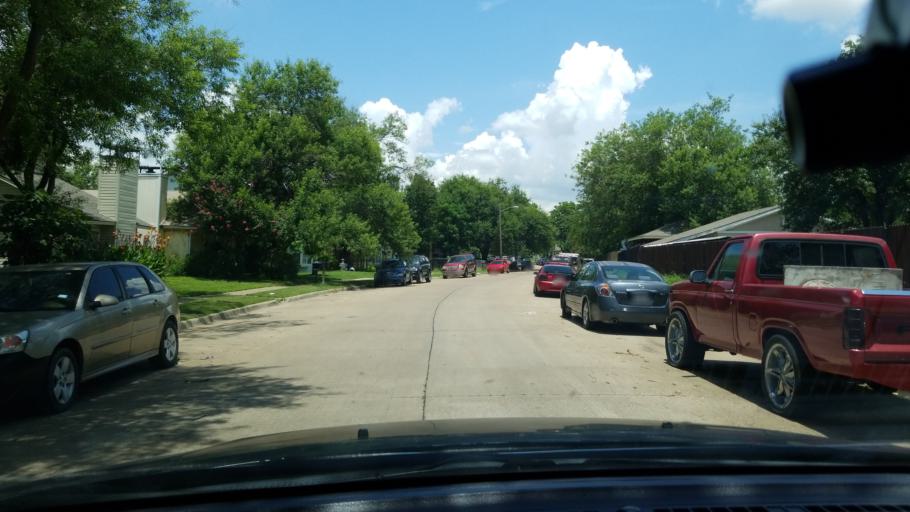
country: US
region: Texas
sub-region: Dallas County
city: Balch Springs
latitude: 32.7489
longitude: -96.6462
